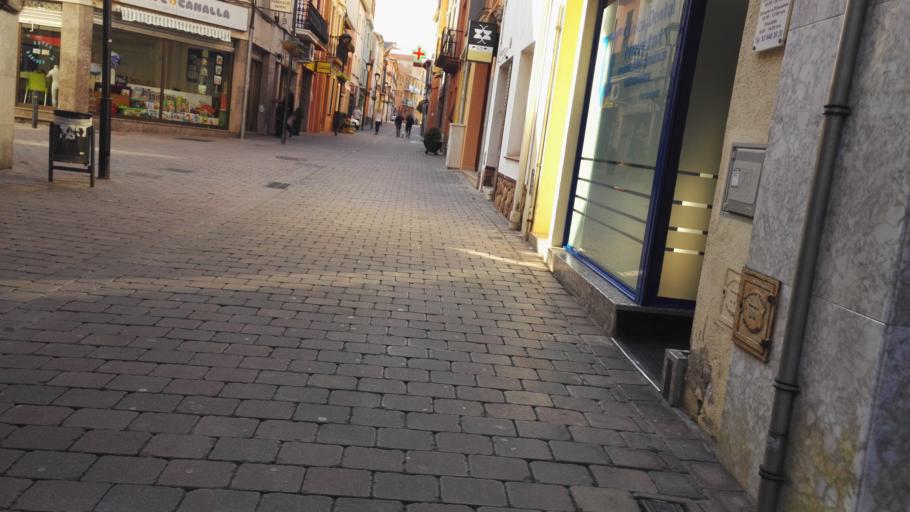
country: ES
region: Catalonia
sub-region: Provincia de Barcelona
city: Santa Maria de Palautordera
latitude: 41.6937
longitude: 2.4444
